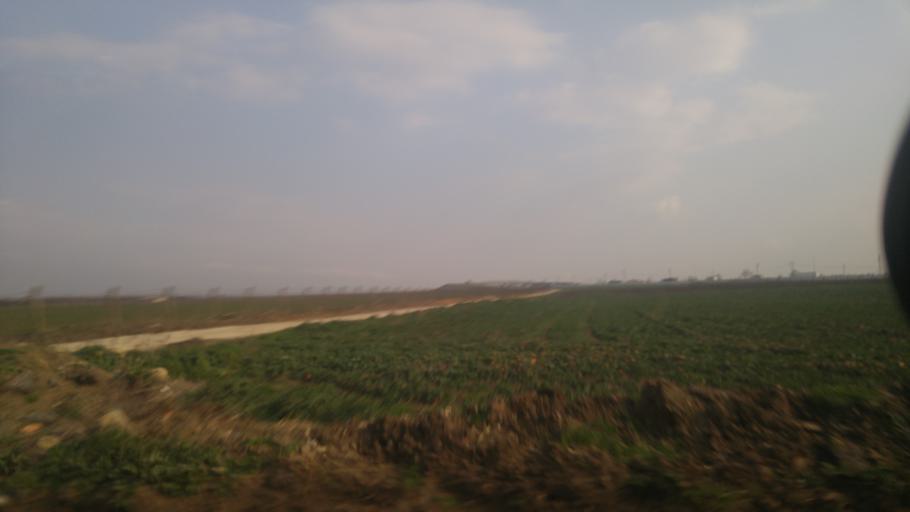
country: TR
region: Istanbul
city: Kavakli
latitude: 41.1093
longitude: 28.2980
